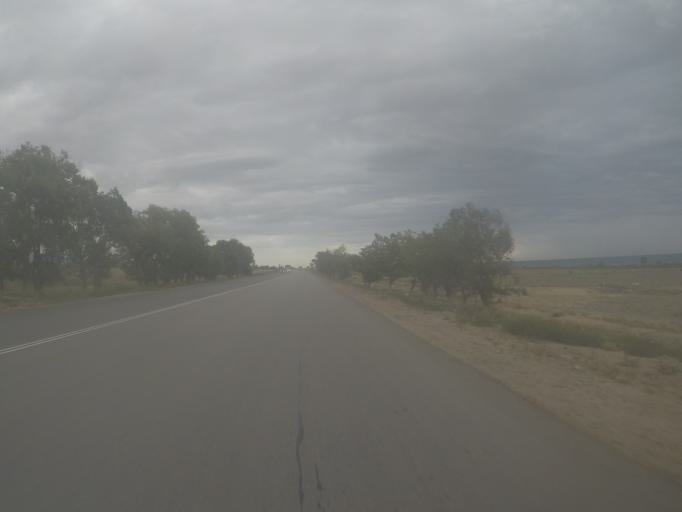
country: KG
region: Ysyk-Koel
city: Cholpon-Ata
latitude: 42.5970
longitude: 76.8387
